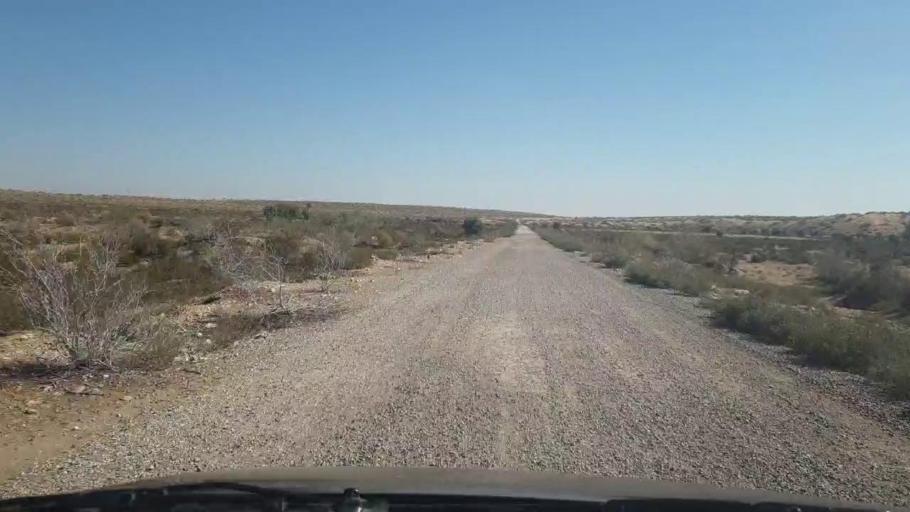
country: PK
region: Sindh
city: Bozdar
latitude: 27.0211
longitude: 68.7211
